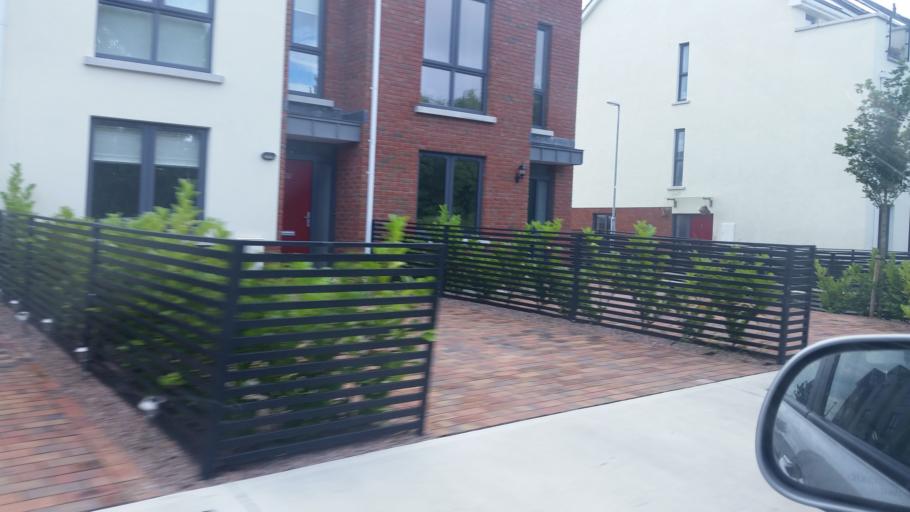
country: IE
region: Leinster
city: Donaghmede
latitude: 53.4047
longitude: -6.1581
